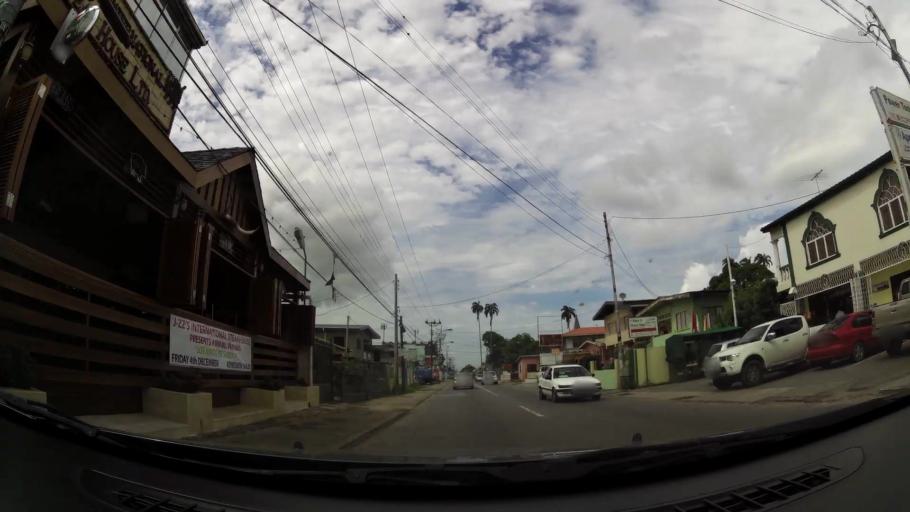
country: TT
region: Couva-Tabaquite-Talparo
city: Couva
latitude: 10.4226
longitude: -61.4702
